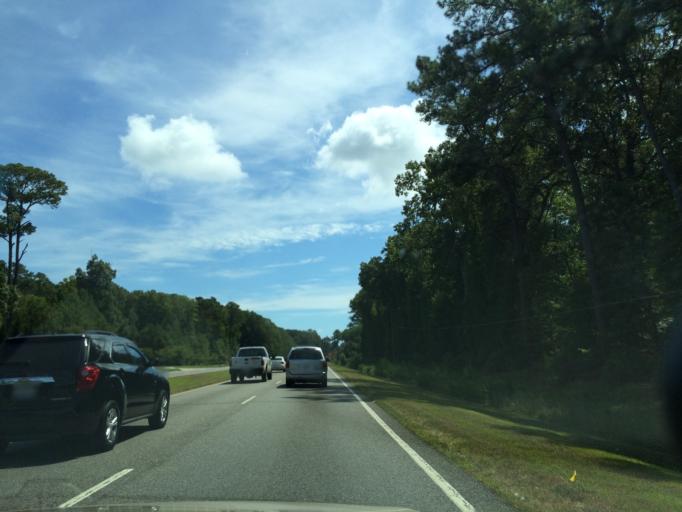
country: US
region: Virginia
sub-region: York County
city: Yorktown
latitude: 37.2004
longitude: -76.4976
